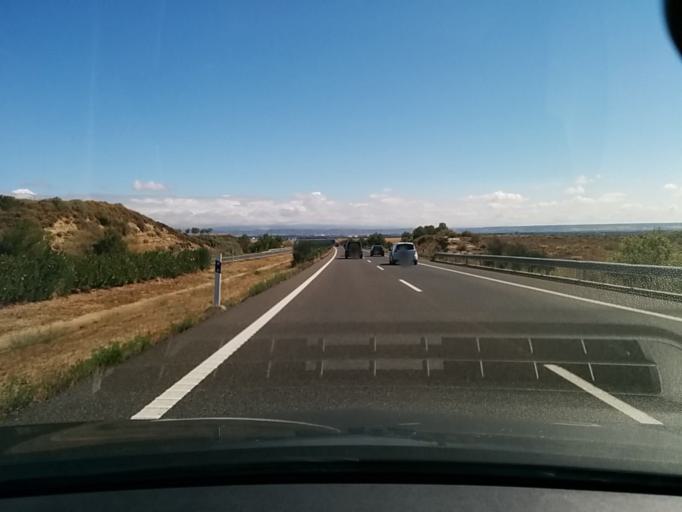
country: ES
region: Aragon
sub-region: Provincia de Huesca
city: Sangarren
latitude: 42.0769
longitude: -0.4959
